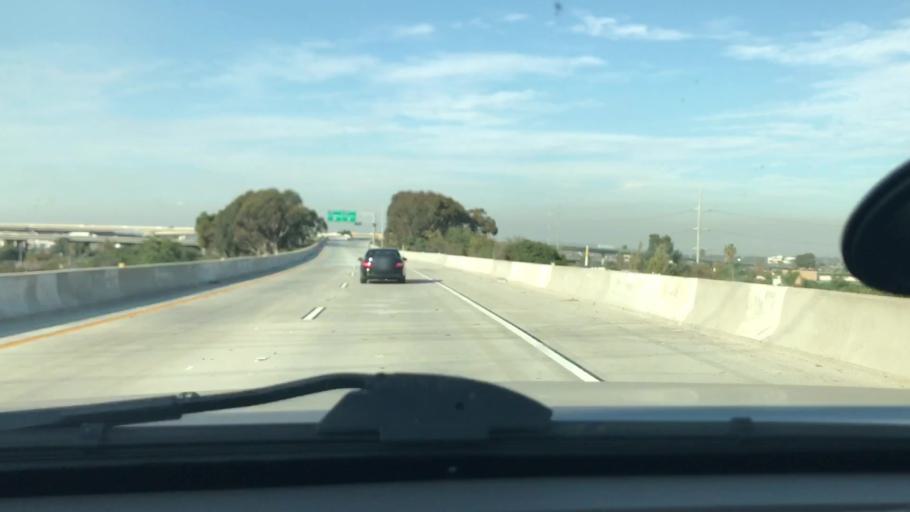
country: US
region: California
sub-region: Los Angeles County
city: Del Aire
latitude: 33.9237
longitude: -118.3678
